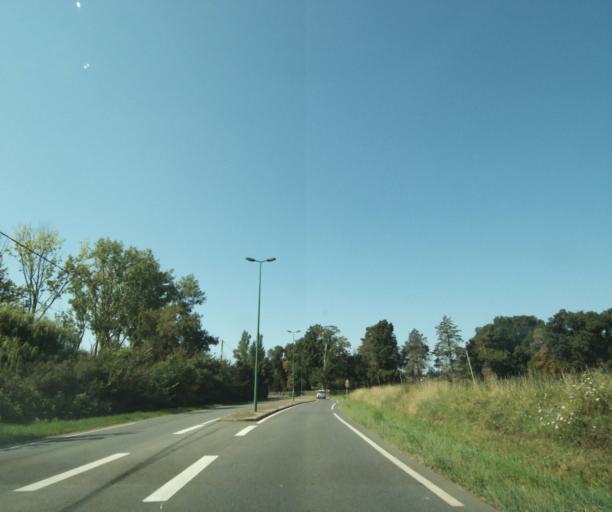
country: FR
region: Midi-Pyrenees
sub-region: Departement de la Haute-Garonne
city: Beaumont-sur-Leze
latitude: 43.3873
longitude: 1.3489
